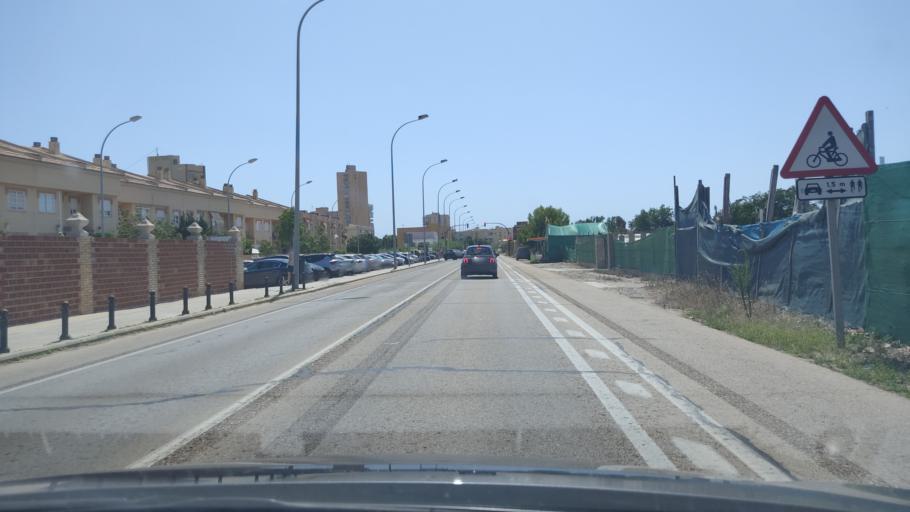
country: ES
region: Valencia
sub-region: Provincia de Valencia
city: Sollana
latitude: 39.3059
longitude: -0.2954
